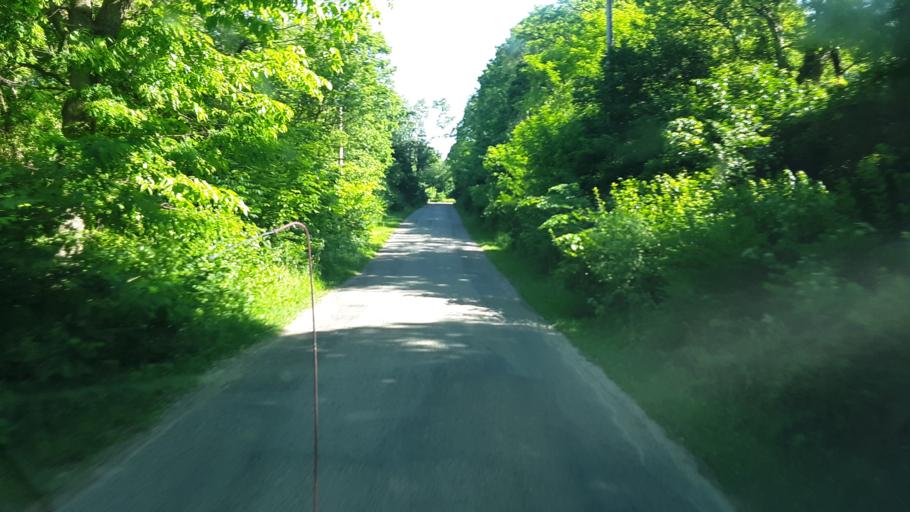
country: US
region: Ohio
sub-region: Preble County
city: New Paris
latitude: 39.8714
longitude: -84.8324
